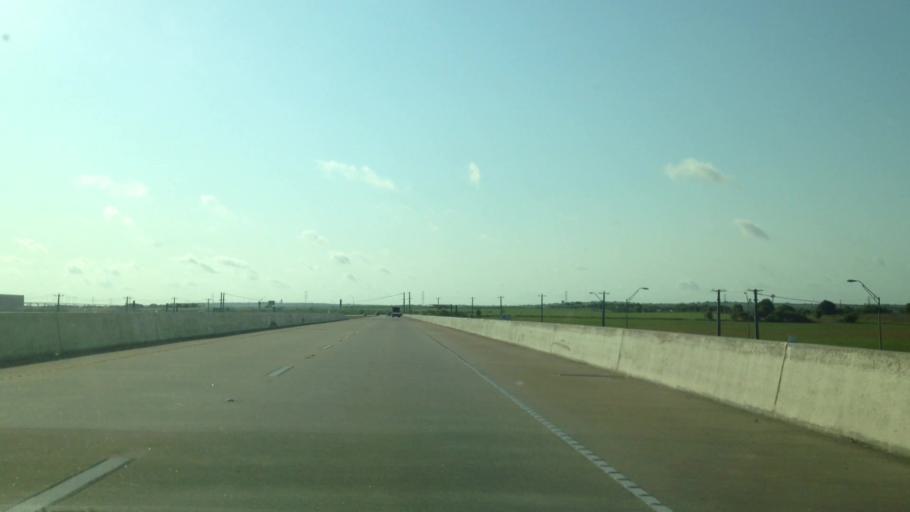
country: US
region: Texas
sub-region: Travis County
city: Onion Creek
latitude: 30.0838
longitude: -97.7362
